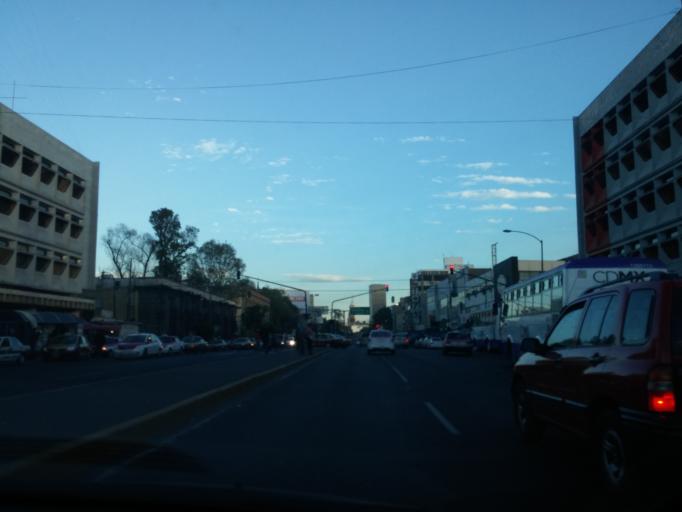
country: MX
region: Mexico City
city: Cuauhtemoc
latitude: 19.4420
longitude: -99.1610
